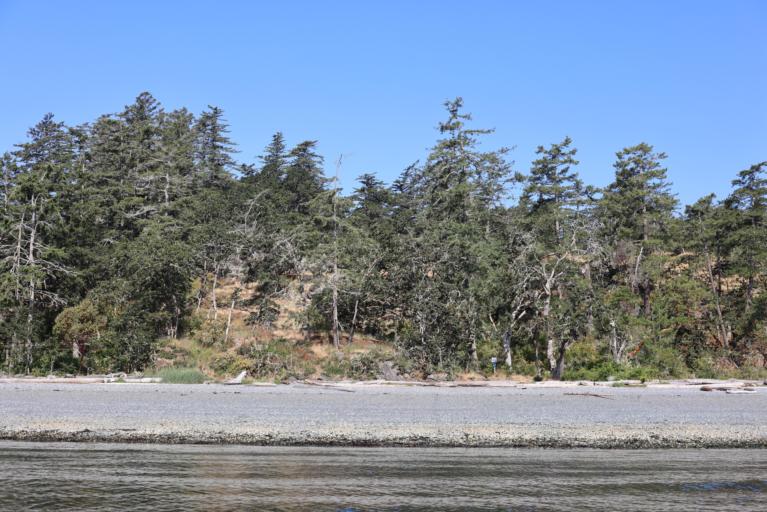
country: CA
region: British Columbia
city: Metchosin
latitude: 48.3619
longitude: -123.5333
